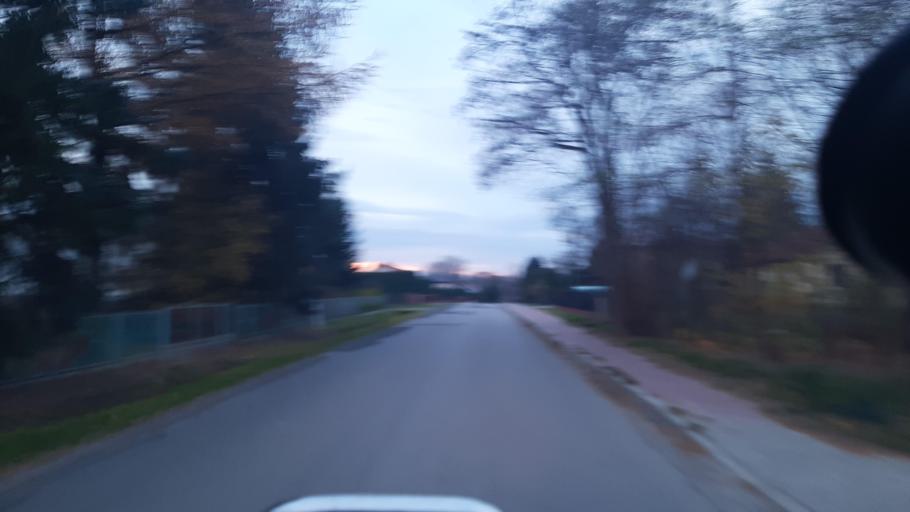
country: PL
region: Lublin Voivodeship
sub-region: Powiat lubelski
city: Garbow
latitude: 51.3585
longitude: 22.3737
